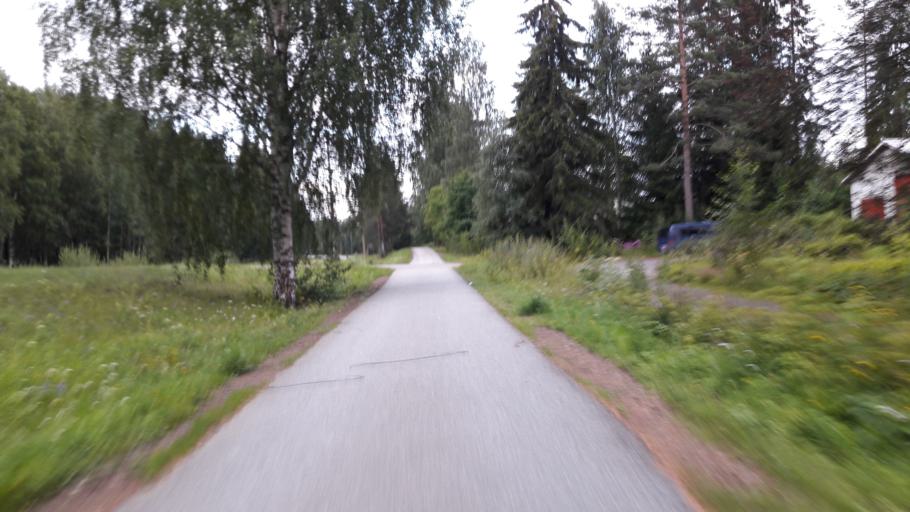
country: FI
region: North Karelia
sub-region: Joensuu
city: Joensuu
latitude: 62.5242
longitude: 29.8571
